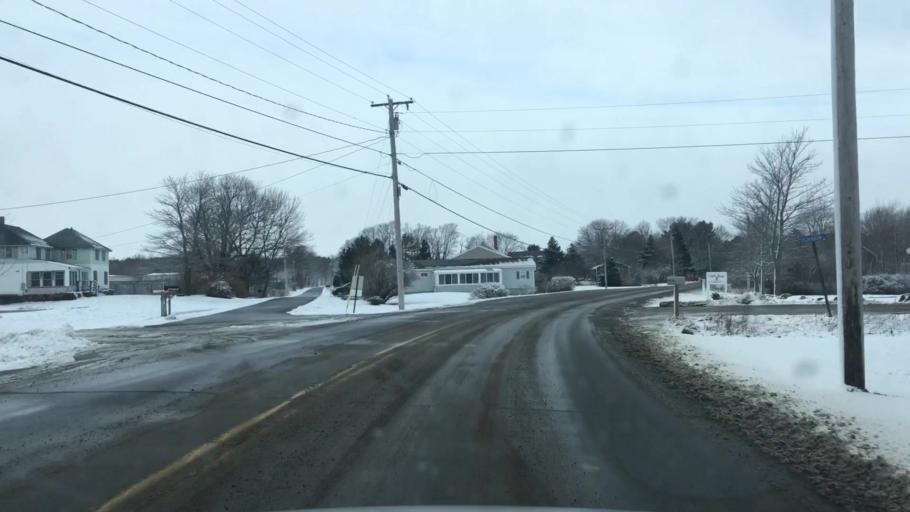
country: US
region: Maine
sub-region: Knox County
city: South Thomaston
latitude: 44.0626
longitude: -69.0926
